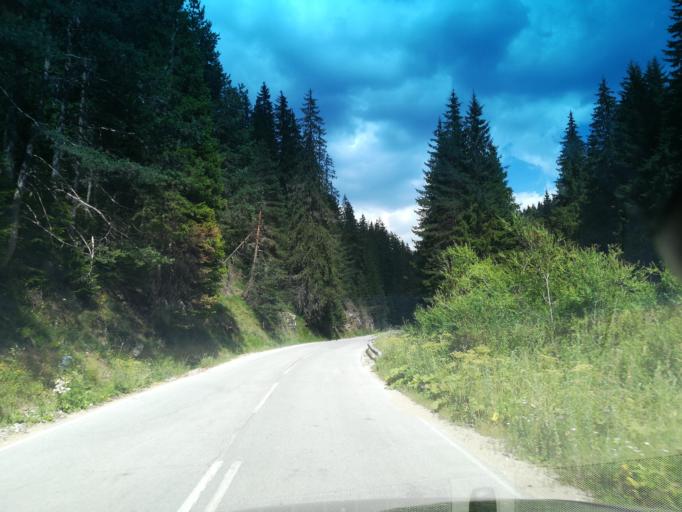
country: BG
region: Smolyan
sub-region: Obshtina Chepelare
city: Chepelare
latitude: 41.6618
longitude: 24.6501
